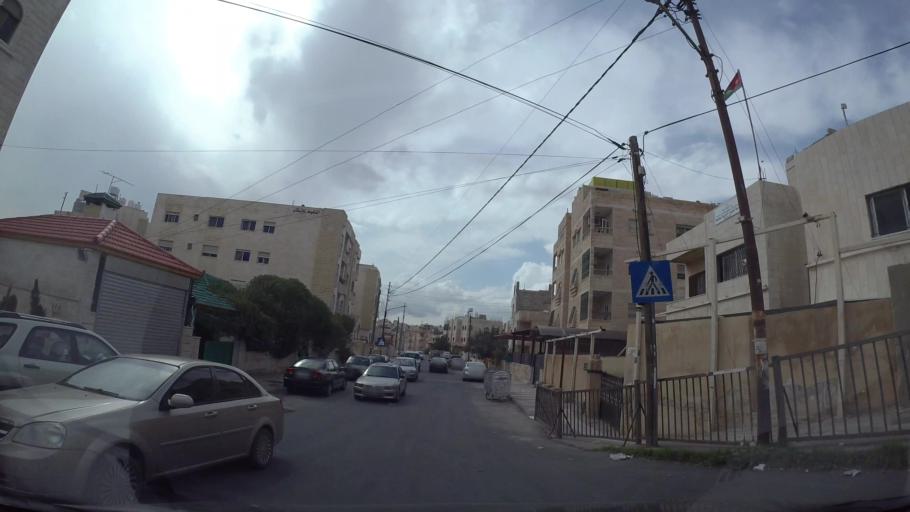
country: JO
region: Amman
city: Amman
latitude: 31.9986
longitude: 35.9417
